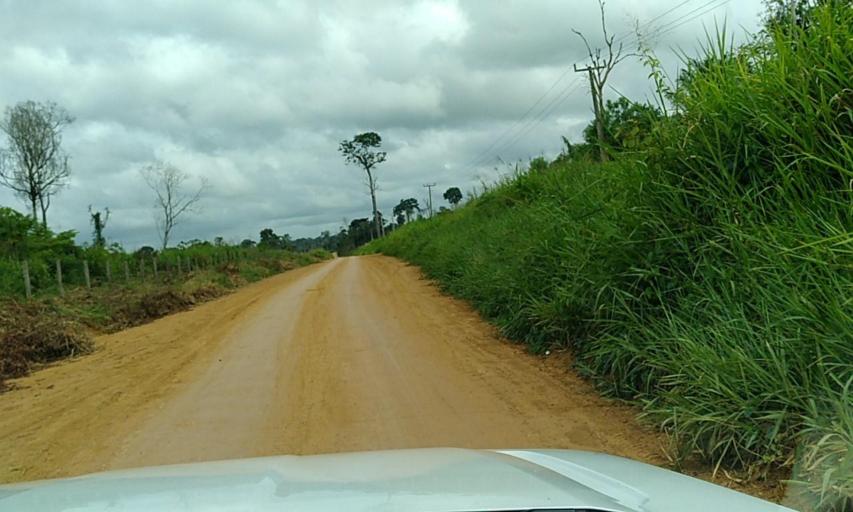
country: BR
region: Para
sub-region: Senador Jose Porfirio
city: Senador Jose Porfirio
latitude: -2.7714
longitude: -51.7807
